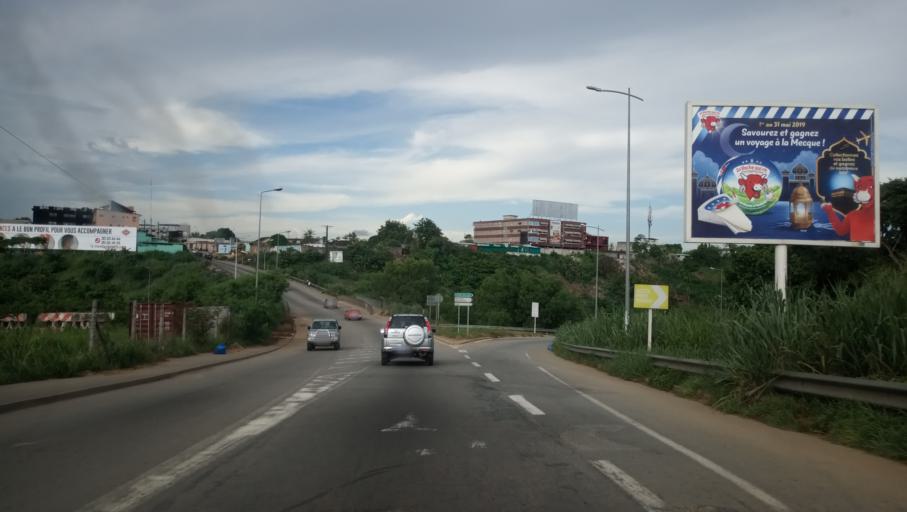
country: CI
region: Lagunes
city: Abidjan
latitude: 5.3492
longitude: -3.9838
